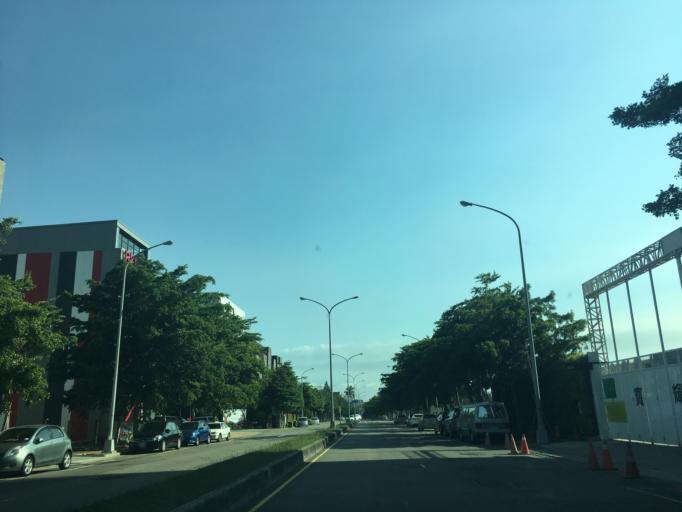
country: TW
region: Taiwan
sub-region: Taichung City
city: Taichung
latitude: 24.1572
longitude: 120.6286
